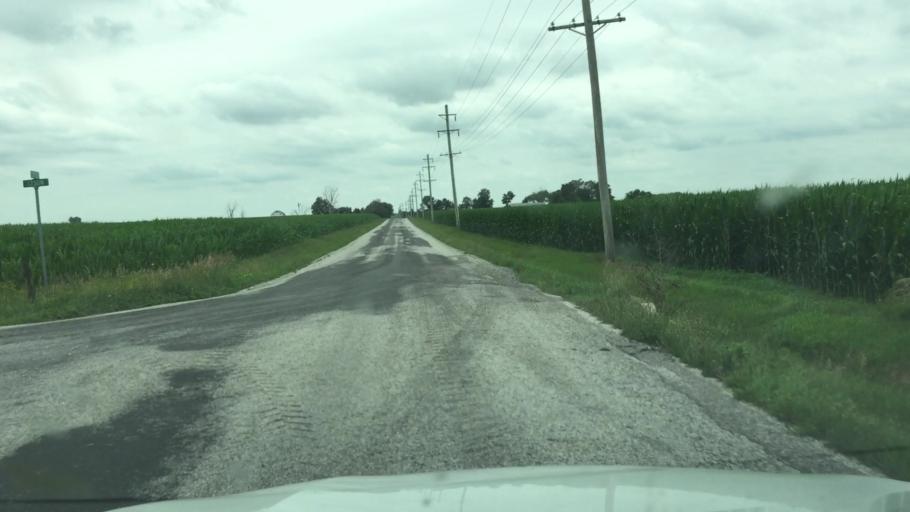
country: US
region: Illinois
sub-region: Hancock County
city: Carthage
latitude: 40.3935
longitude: -91.0826
